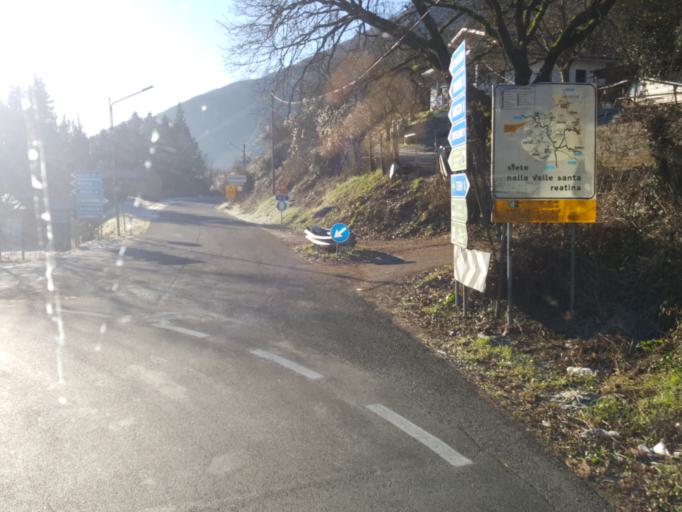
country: IT
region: Latium
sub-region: Provincia di Rieti
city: Colli sul Velino
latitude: 42.5056
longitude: 12.7401
